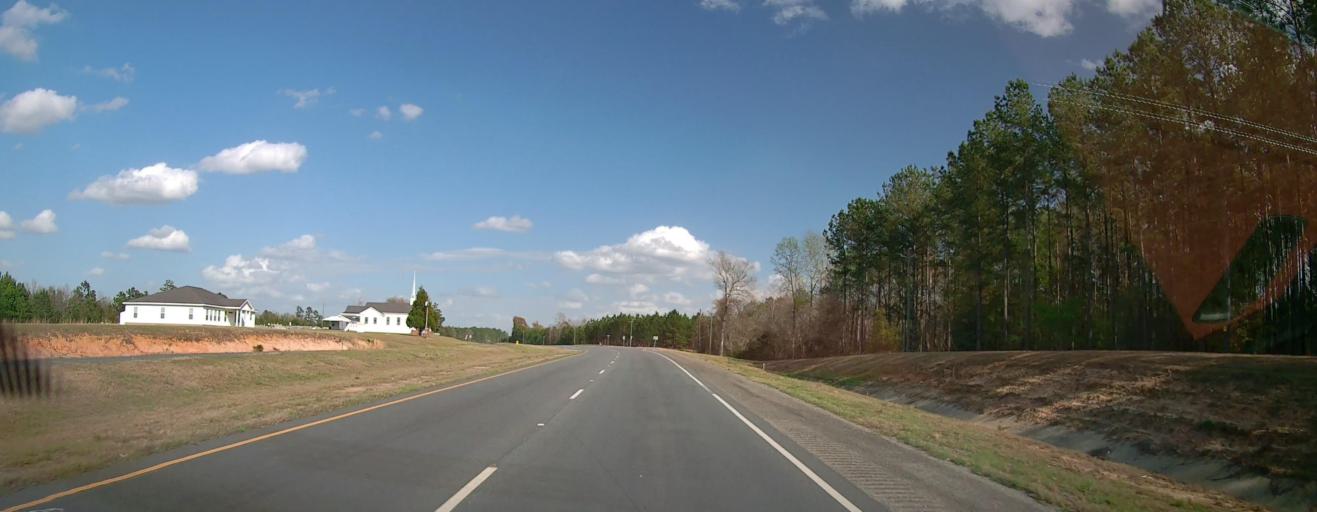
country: US
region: Georgia
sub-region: Telfair County
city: Helena
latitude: 32.1027
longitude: -83.0148
